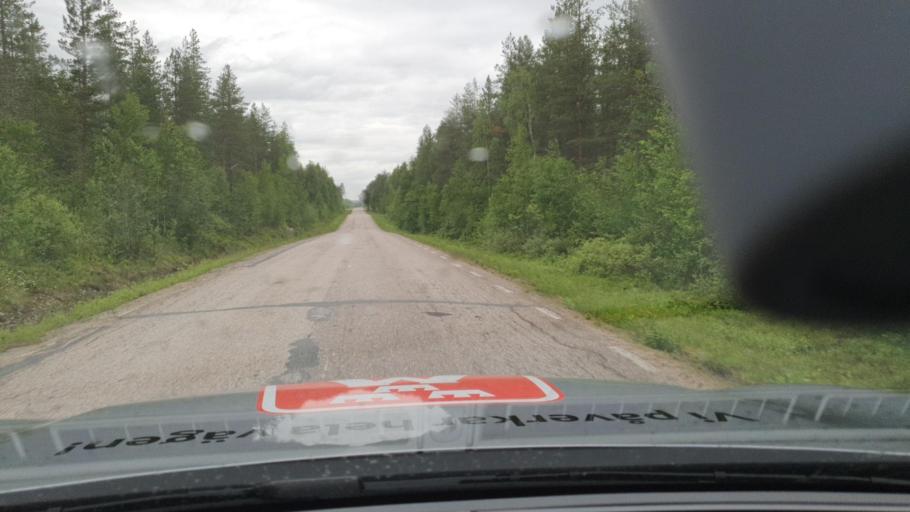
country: SE
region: Norrbotten
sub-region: Overkalix Kommun
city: OEverkalix
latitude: 66.3826
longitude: 22.7936
